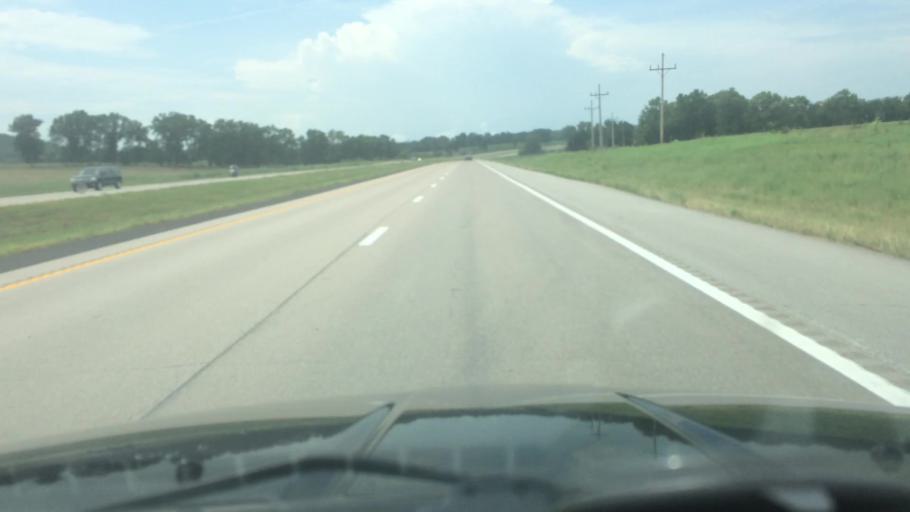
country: US
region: Missouri
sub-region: Polk County
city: Humansville
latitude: 37.8172
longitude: -93.6111
